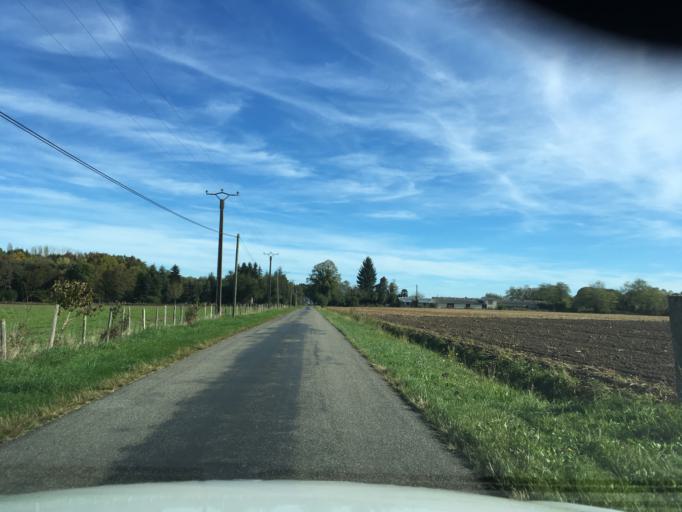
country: FR
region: Aquitaine
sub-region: Departement des Pyrenees-Atlantiques
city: Buros
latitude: 43.3308
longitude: -0.3301
